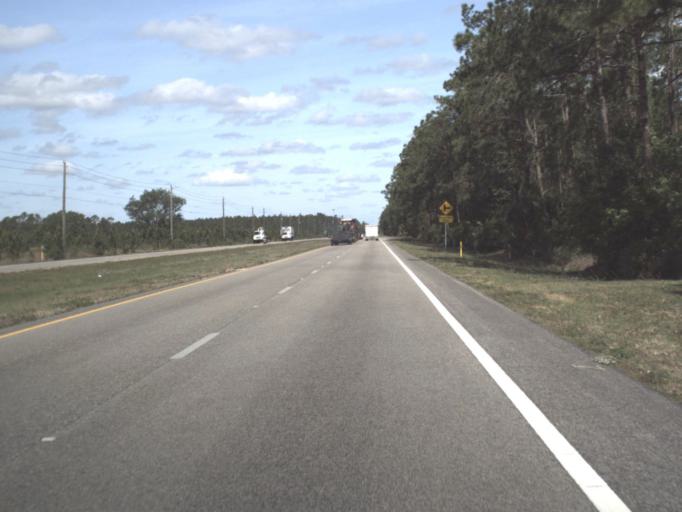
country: US
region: Florida
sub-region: Volusia County
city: Ormond-by-the-Sea
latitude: 29.3573
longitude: -81.1600
